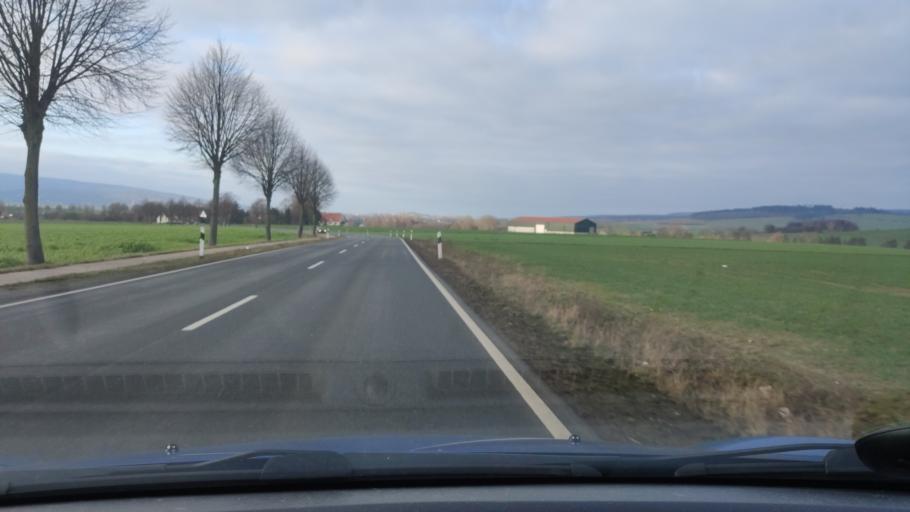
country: DE
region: Lower Saxony
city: Coppenbrugge
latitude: 52.1483
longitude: 9.5065
